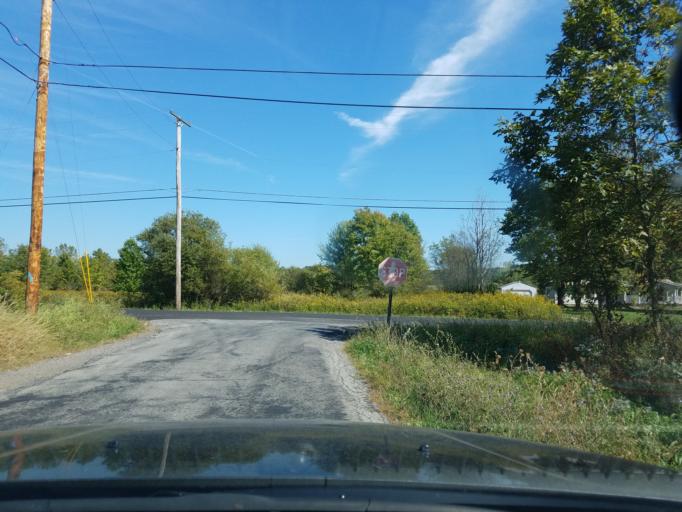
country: US
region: Pennsylvania
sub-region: Lawrence County
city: Ellwood City
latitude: 40.9334
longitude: -80.3039
